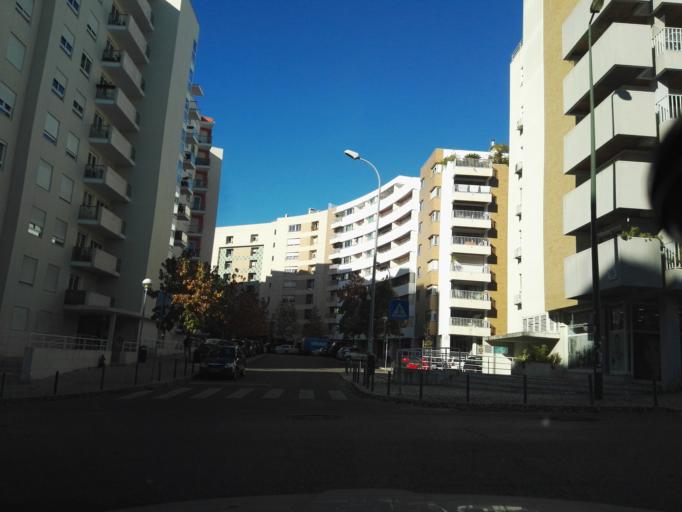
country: PT
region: Lisbon
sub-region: Odivelas
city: Olival do Basto
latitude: 38.7666
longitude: -9.1529
